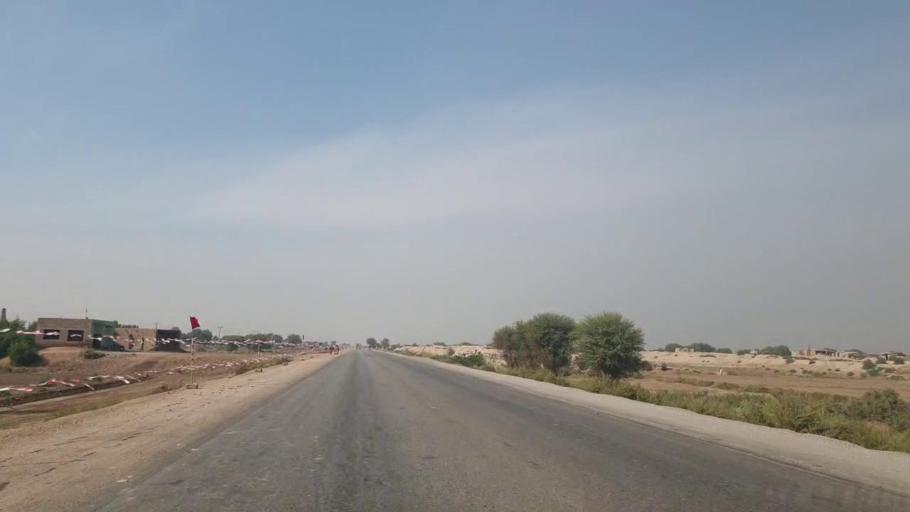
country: PK
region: Sindh
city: Sann
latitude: 25.9868
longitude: 68.1807
